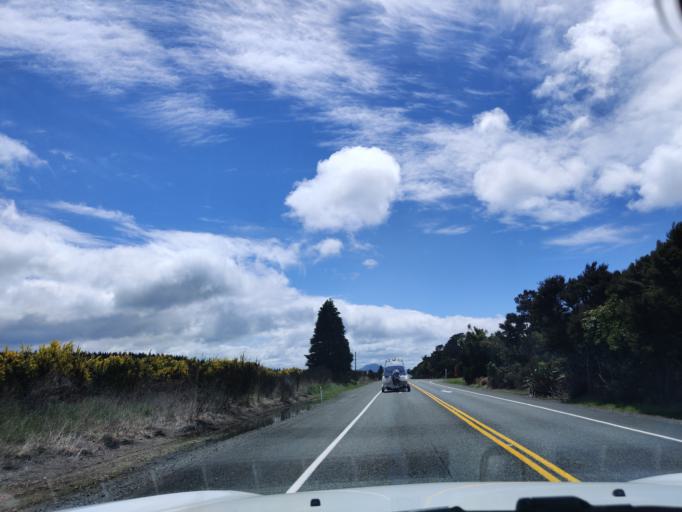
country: NZ
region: Waikato
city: Turangi
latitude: -39.0195
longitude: 175.8087
